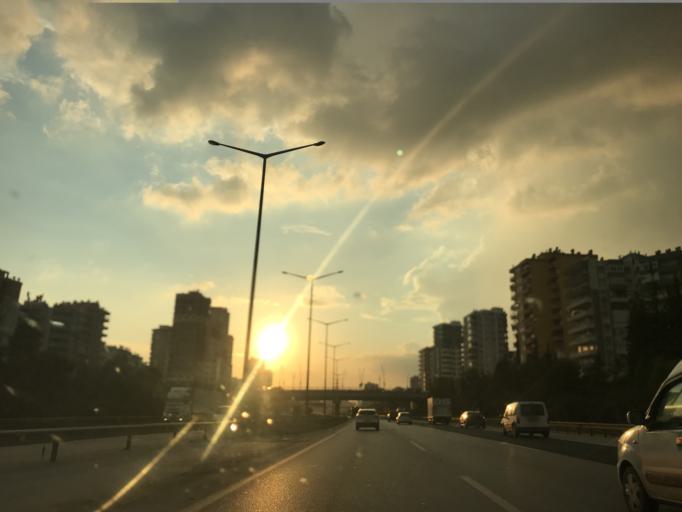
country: TR
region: Adana
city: Seyhan
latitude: 37.0328
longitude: 35.2925
